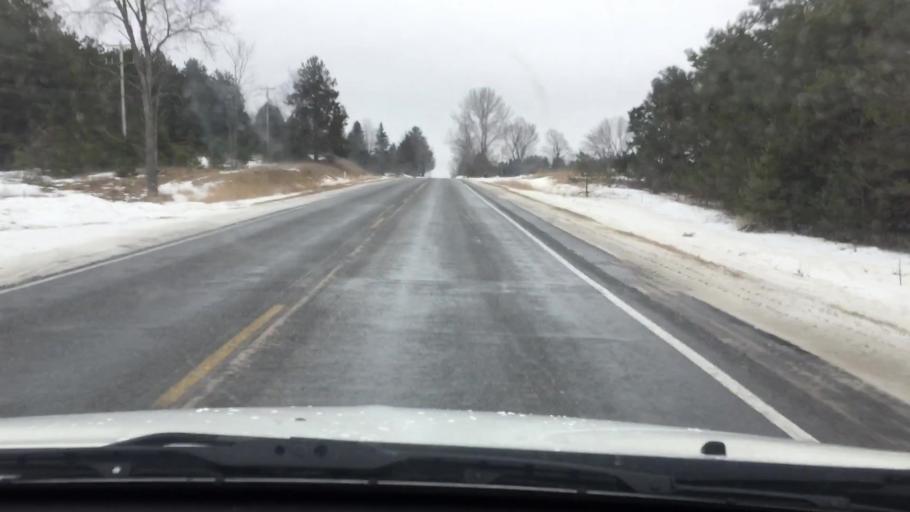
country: US
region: Michigan
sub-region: Wexford County
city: Cadillac
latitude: 44.0709
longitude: -85.4440
